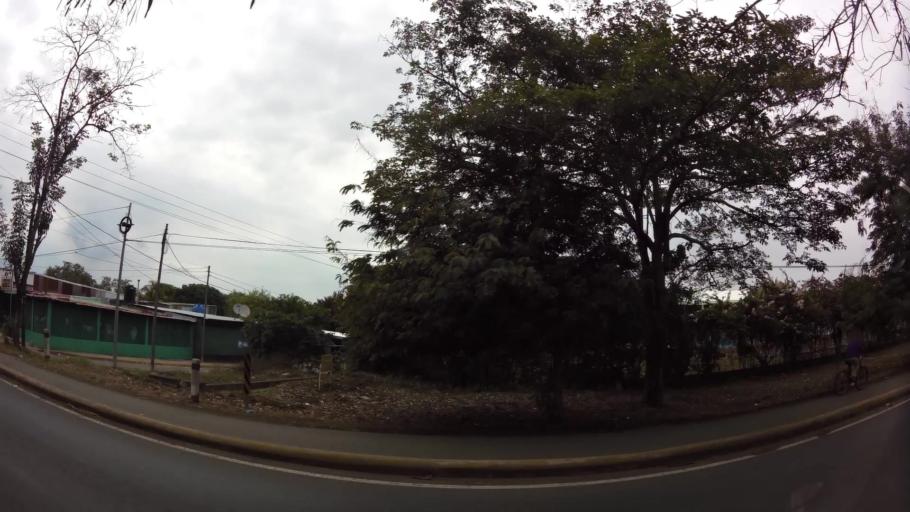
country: NI
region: Masaya
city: Masaya
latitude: 11.9728
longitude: -86.0782
